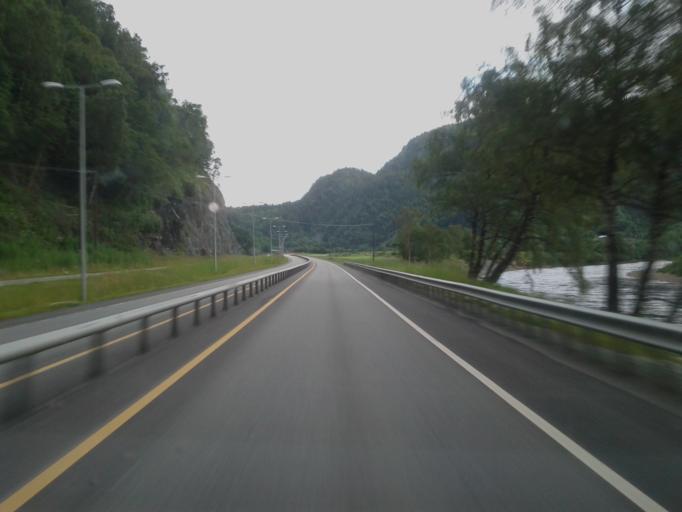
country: NO
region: Sor-Trondelag
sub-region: Midtre Gauldal
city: Storen
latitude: 63.0790
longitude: 10.2587
